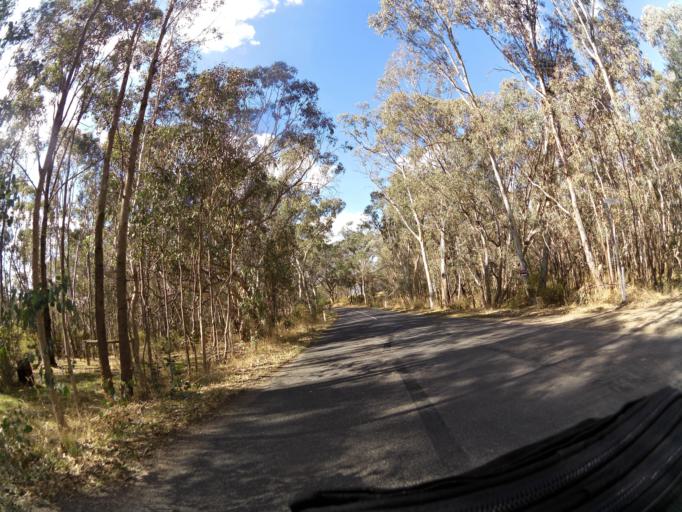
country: AU
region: Victoria
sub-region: Greater Bendigo
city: Kennington
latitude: -36.9545
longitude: 144.7712
